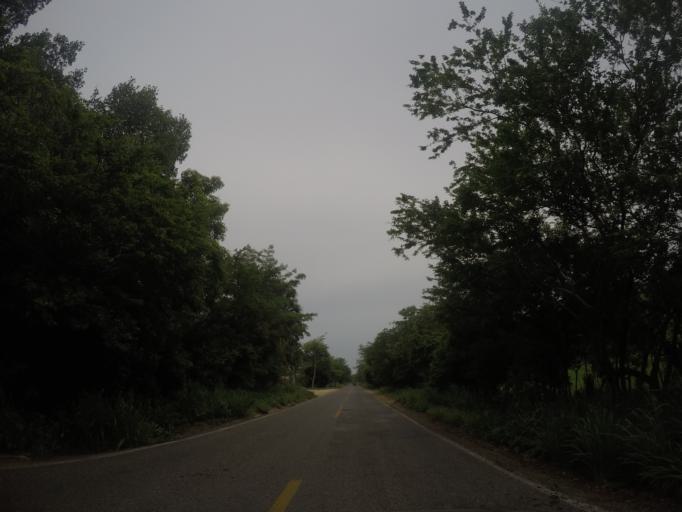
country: MX
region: Oaxaca
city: San Pedro Mixtepec
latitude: 15.9551
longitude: -97.2056
